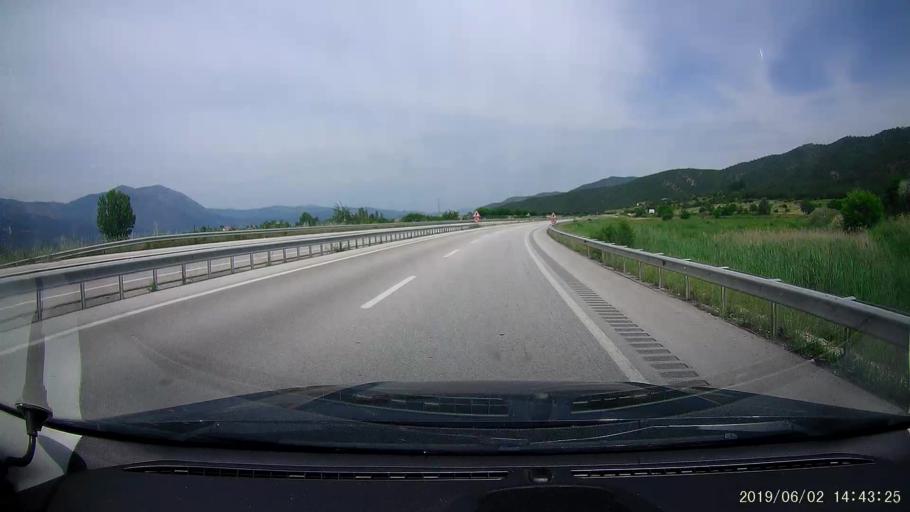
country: TR
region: Corum
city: Hacihamza
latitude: 41.0984
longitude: 34.3853
